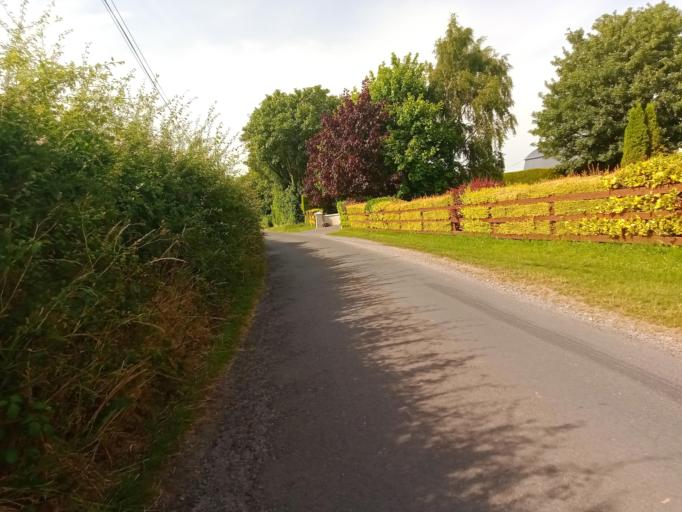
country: IE
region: Leinster
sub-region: Laois
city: Rathdowney
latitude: 52.8125
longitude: -7.4701
